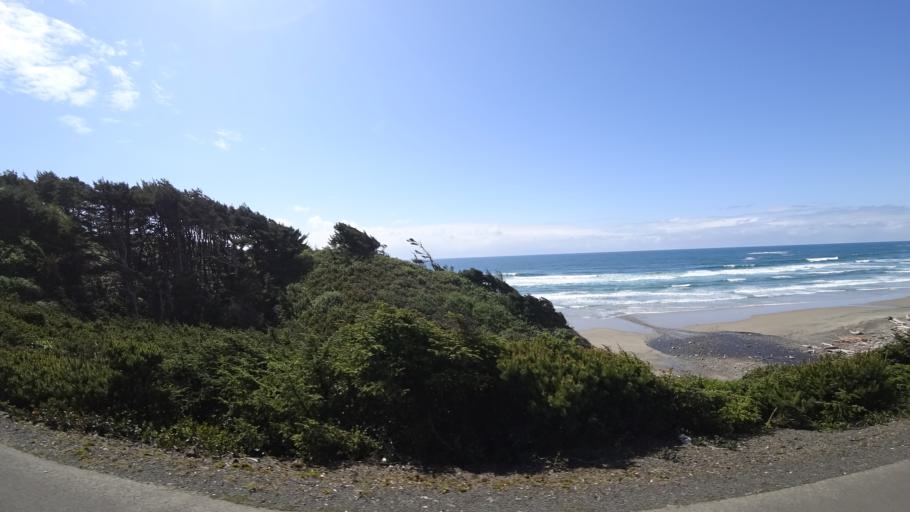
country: US
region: Oregon
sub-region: Lincoln County
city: Newport
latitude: 44.7150
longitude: -124.0582
